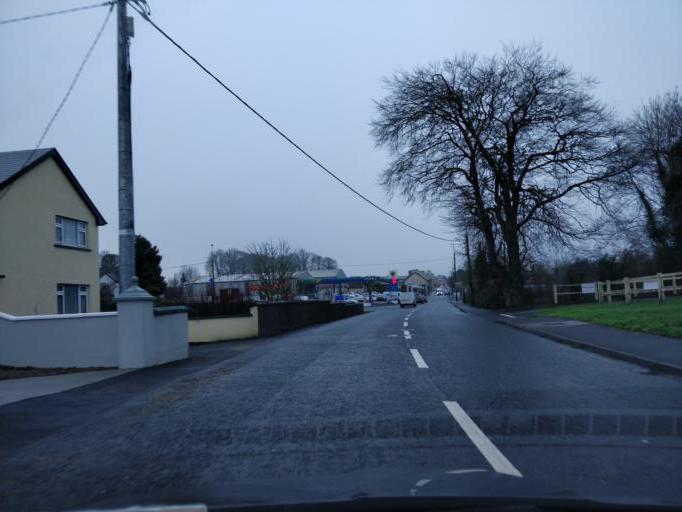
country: IE
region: Connaught
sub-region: Maigh Eo
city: Kiltamagh
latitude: 53.8549
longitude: -8.9947
